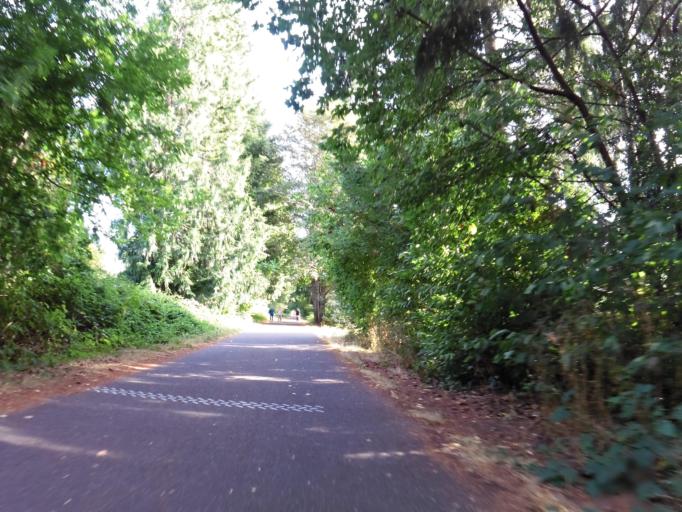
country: US
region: Washington
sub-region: Thurston County
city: Lacey
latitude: 47.0276
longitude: -122.8365
